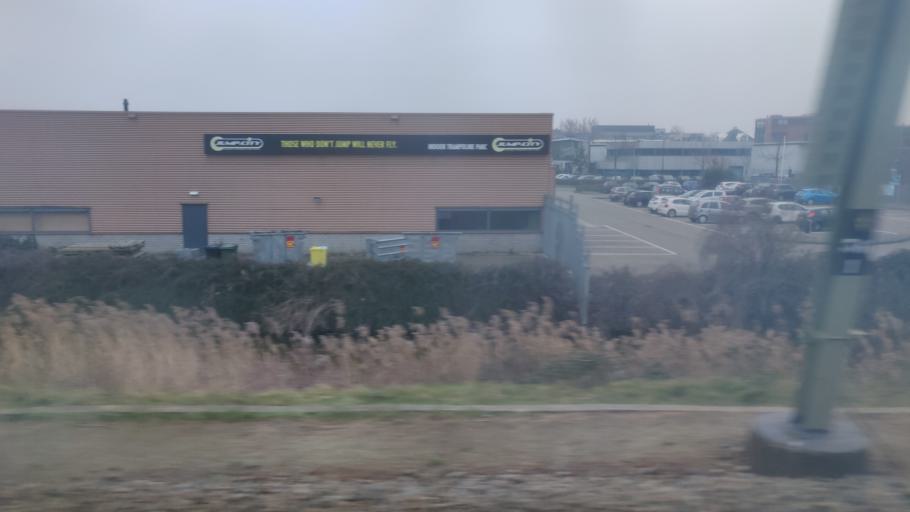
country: NL
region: North Holland
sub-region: Gemeente Langedijk
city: Broek op Langedijk
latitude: 52.6657
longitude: 4.8135
